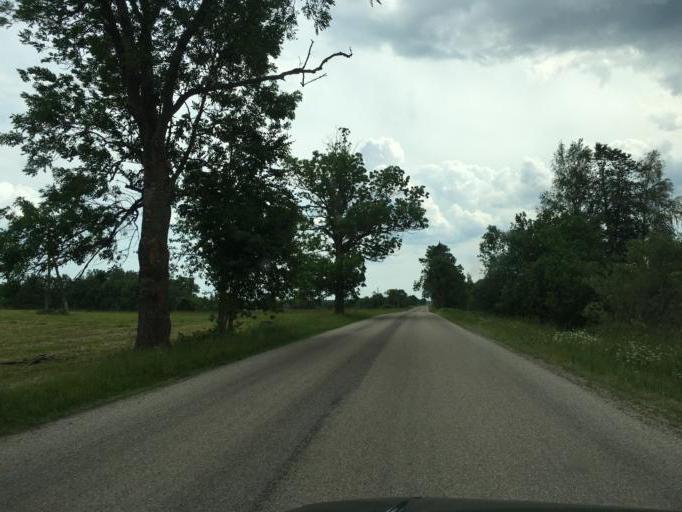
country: LV
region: Rugaju
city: Rugaji
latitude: 56.8992
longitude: 27.0676
